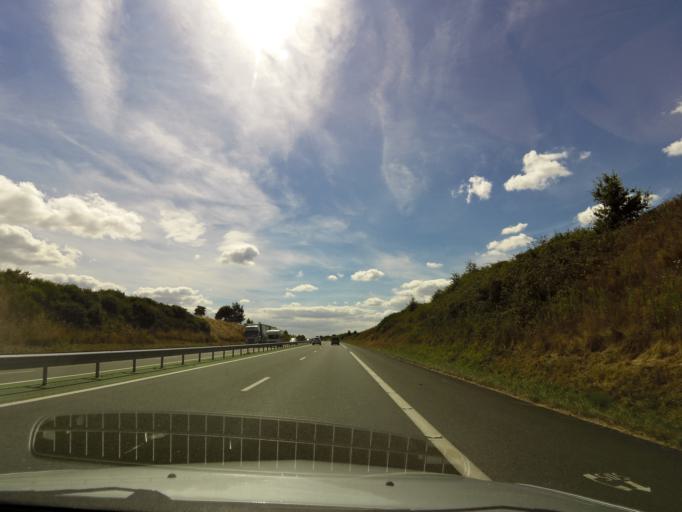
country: FR
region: Pays de la Loire
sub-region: Departement de la Vendee
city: Les Essarts
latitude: 46.7901
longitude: -1.2426
